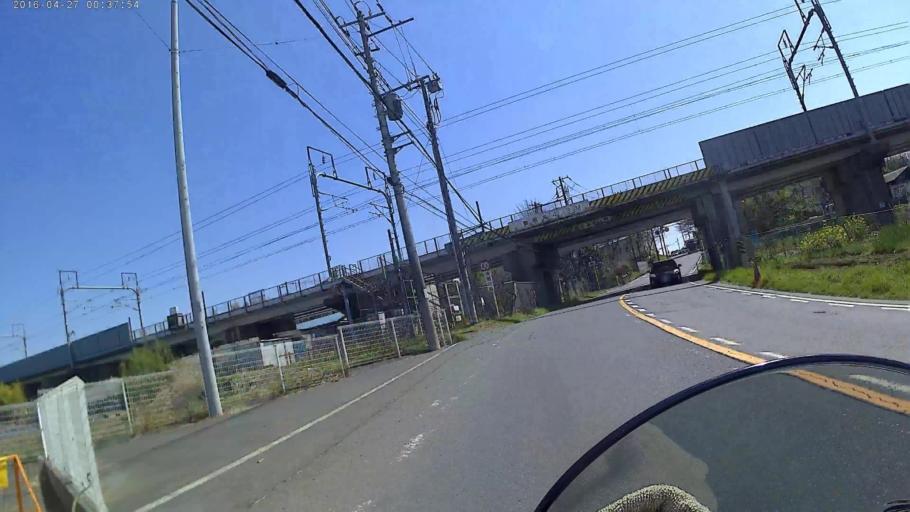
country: JP
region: Kanagawa
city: Atsugi
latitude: 35.4069
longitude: 139.4084
